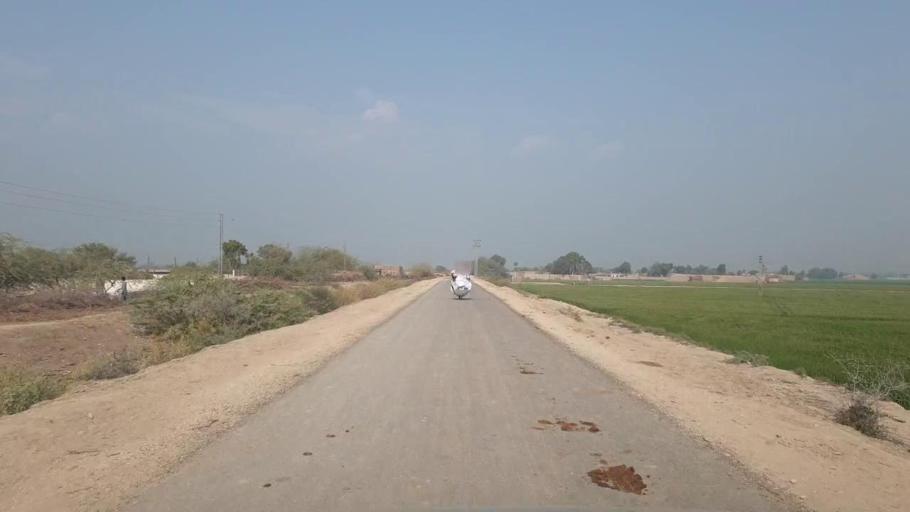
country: PK
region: Sindh
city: Hala
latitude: 25.7974
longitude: 68.4011
